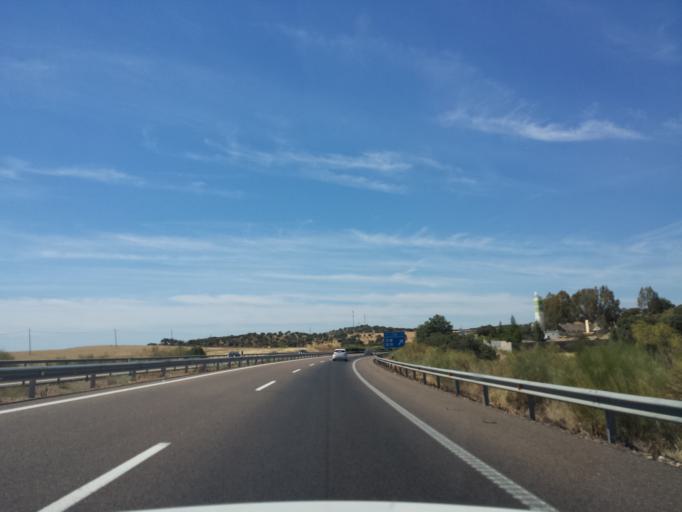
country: ES
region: Extremadura
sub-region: Provincia de Badajoz
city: San Pedro de Merida
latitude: 38.9522
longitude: -6.1660
